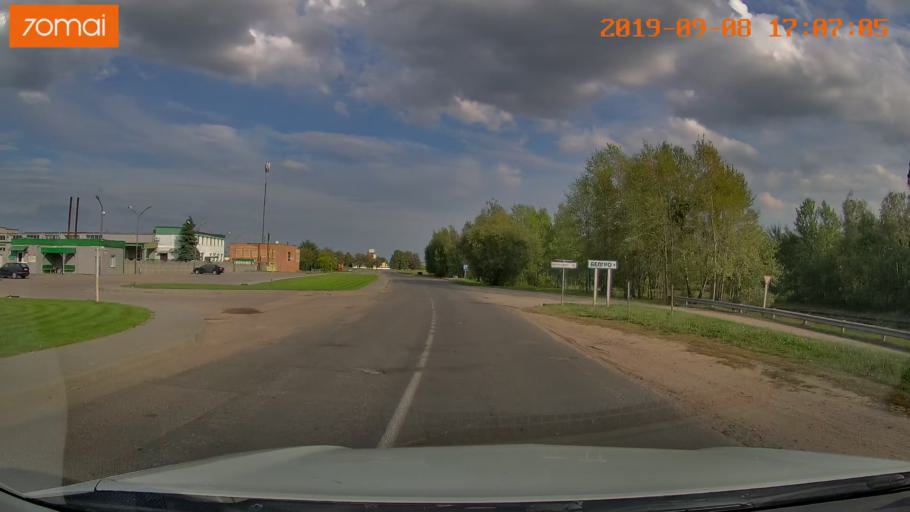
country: BY
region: Grodnenskaya
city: Hrodna
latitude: 53.6659
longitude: 23.9562
